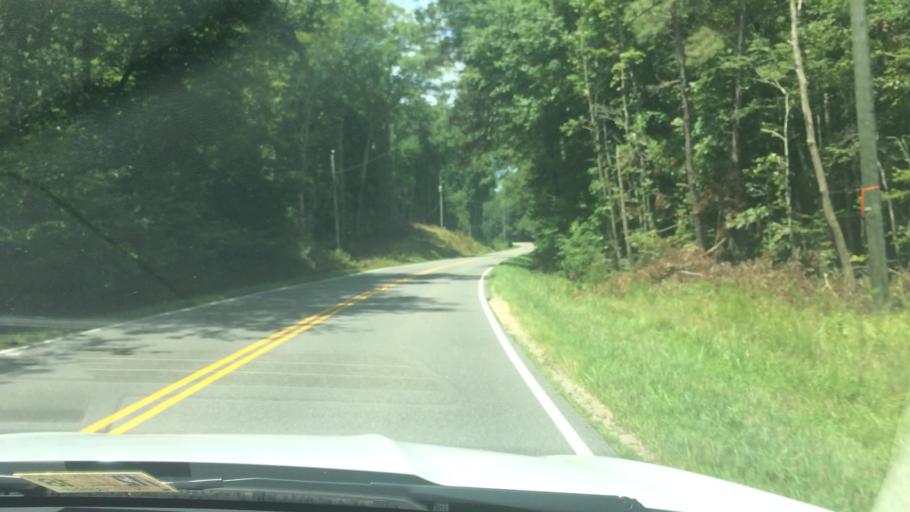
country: US
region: Virginia
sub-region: James City County
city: Williamsburg
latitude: 37.2788
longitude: -76.7896
